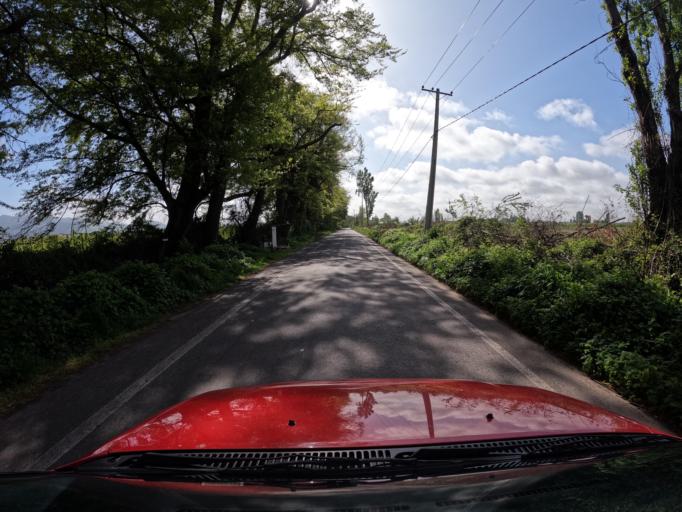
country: CL
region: Maule
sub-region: Provincia de Curico
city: Teno
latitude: -34.8812
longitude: -71.2411
